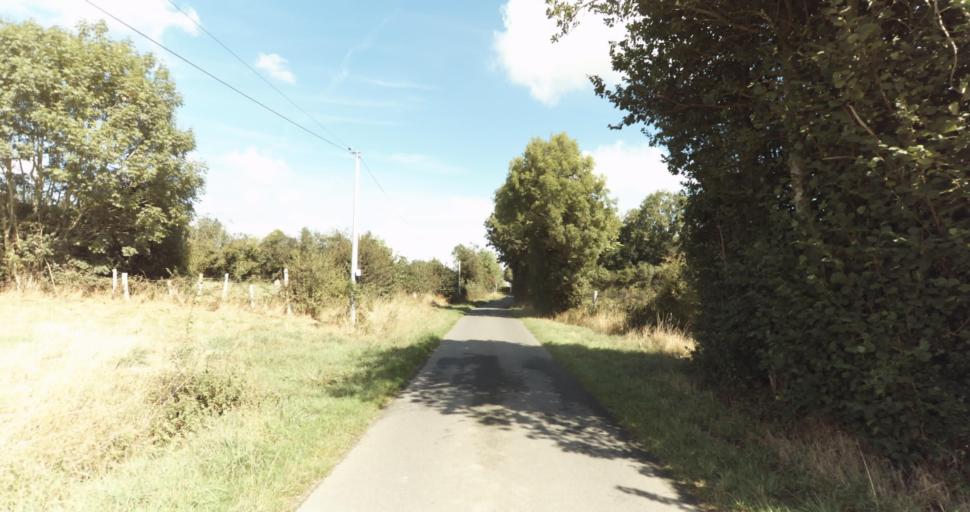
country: FR
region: Lower Normandy
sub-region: Departement du Calvados
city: Orbec
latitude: 48.9413
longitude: 0.3996
